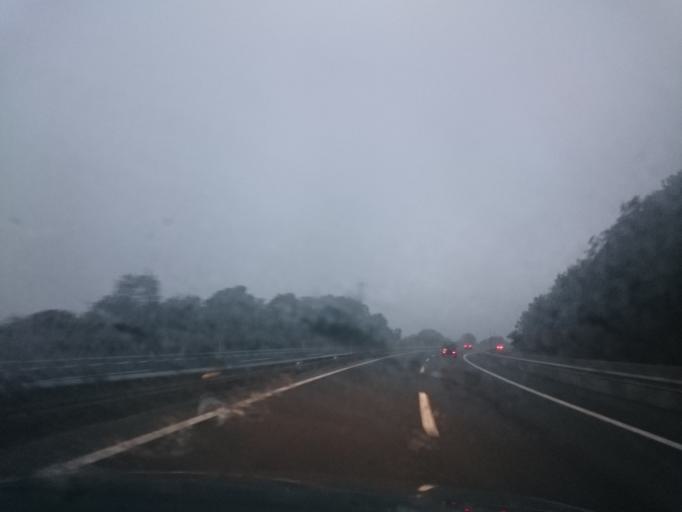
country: ES
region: Asturias
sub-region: Province of Asturias
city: Pola de Lena
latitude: 43.0211
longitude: -5.8230
